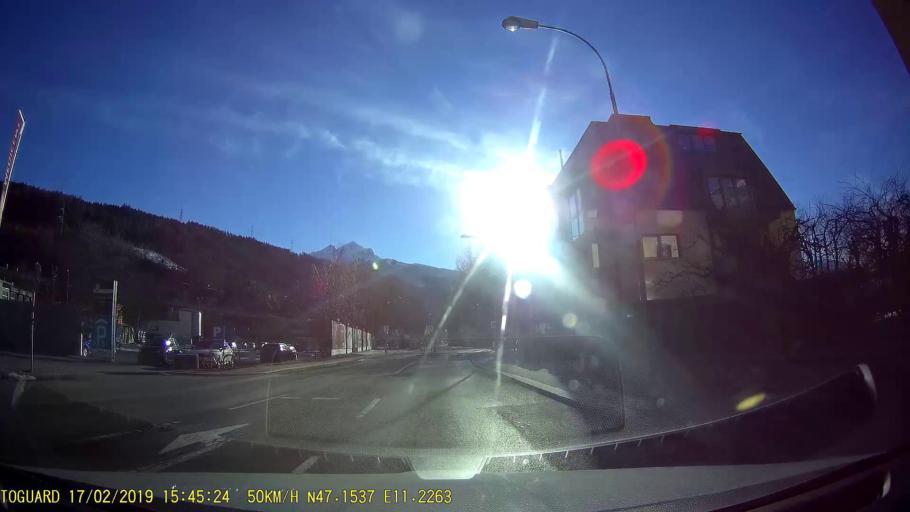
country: AT
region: Tyrol
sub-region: Innsbruck Stadt
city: Innsbruck
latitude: 47.2564
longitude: 11.3774
